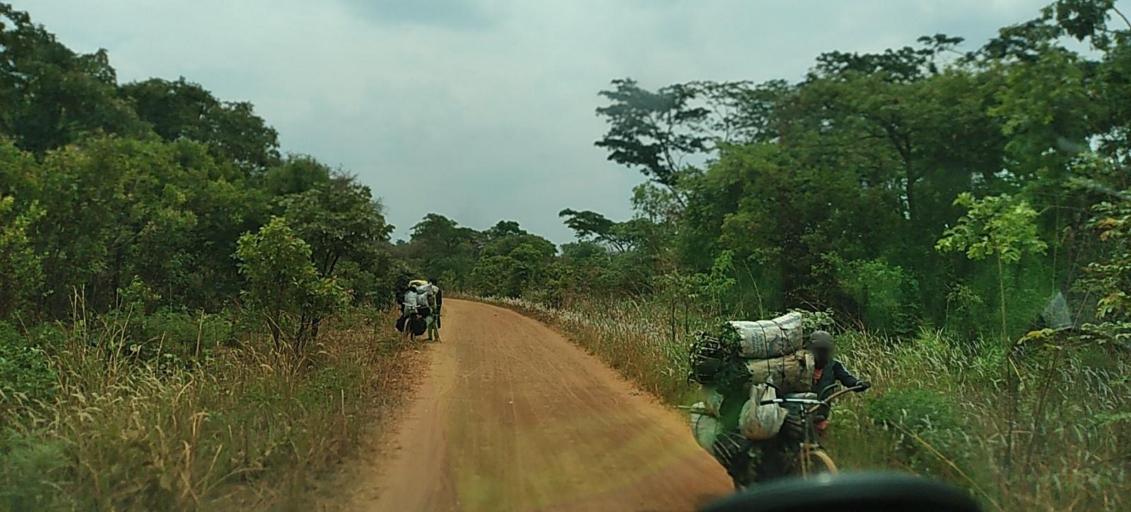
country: ZM
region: North-Western
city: Kansanshi
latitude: -12.0610
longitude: 26.3507
